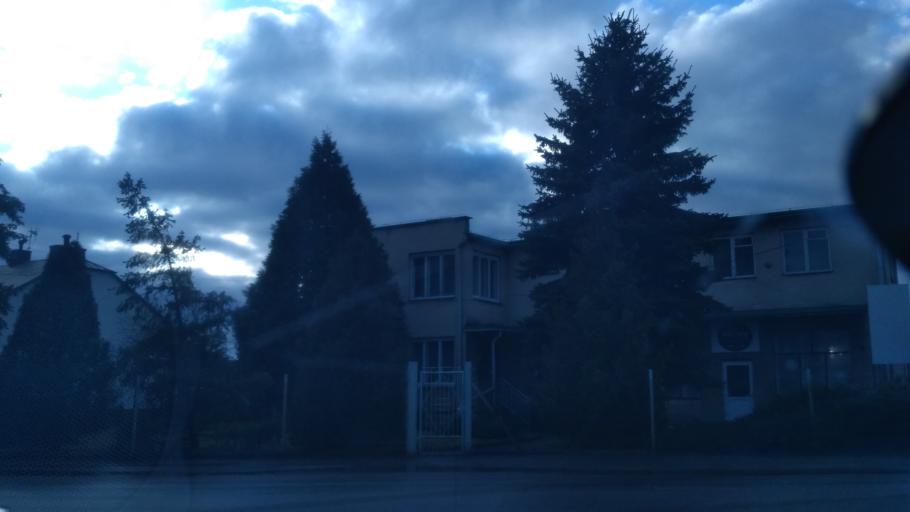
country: PL
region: Subcarpathian Voivodeship
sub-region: Powiat lancucki
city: Czarna
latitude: 50.1116
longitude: 22.1804
